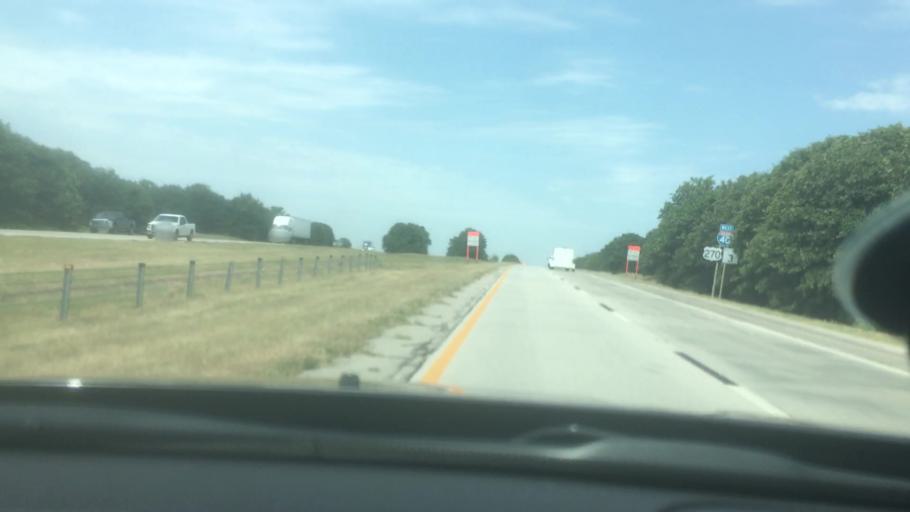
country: US
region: Oklahoma
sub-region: Pottawatomie County
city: McLoud
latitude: 35.3844
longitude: -97.1676
